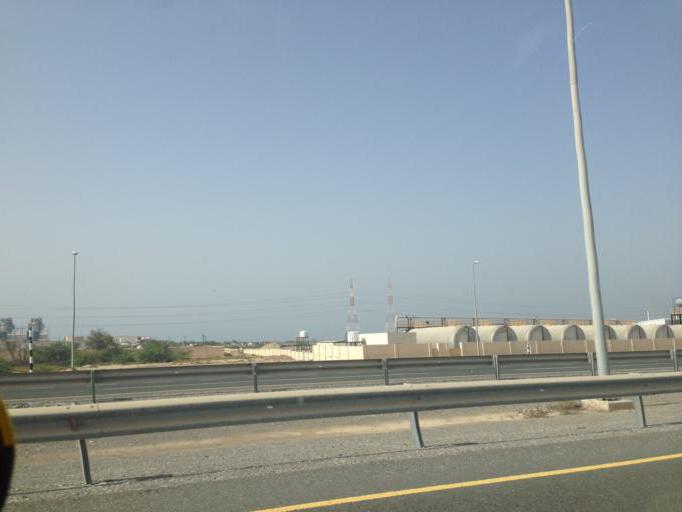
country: OM
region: Al Batinah
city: Barka'
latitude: 23.6994
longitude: 57.9857
